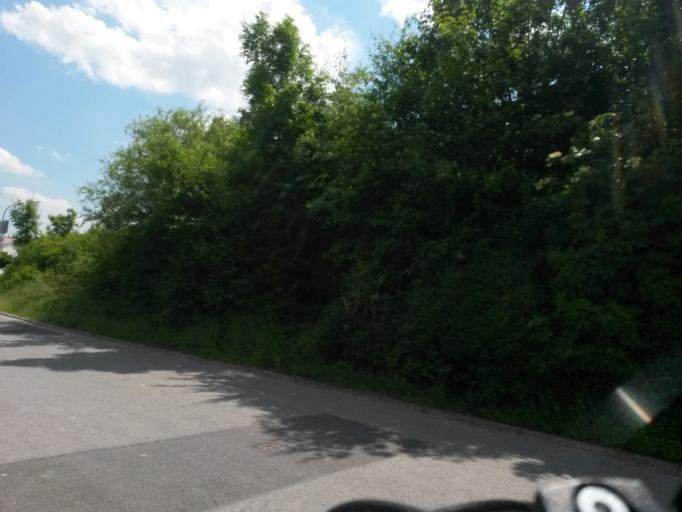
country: DE
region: Bavaria
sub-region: Regierungsbezirk Unterfranken
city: Euerdorf
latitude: 50.1500
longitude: 10.0180
